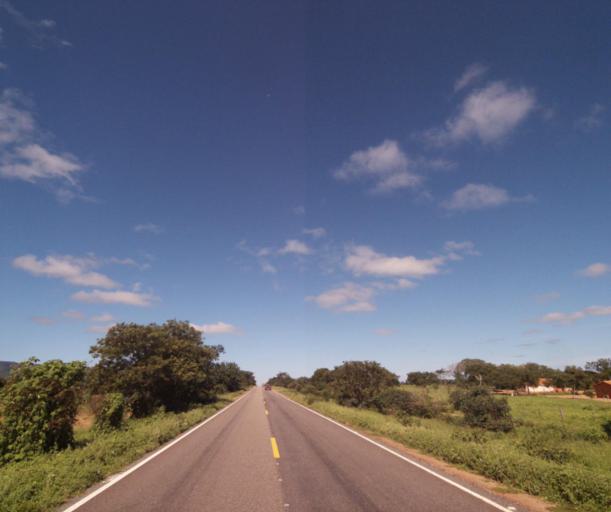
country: BR
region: Bahia
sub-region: Palmas De Monte Alto
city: Palmas de Monte Alto
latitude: -14.2412
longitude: -43.0586
